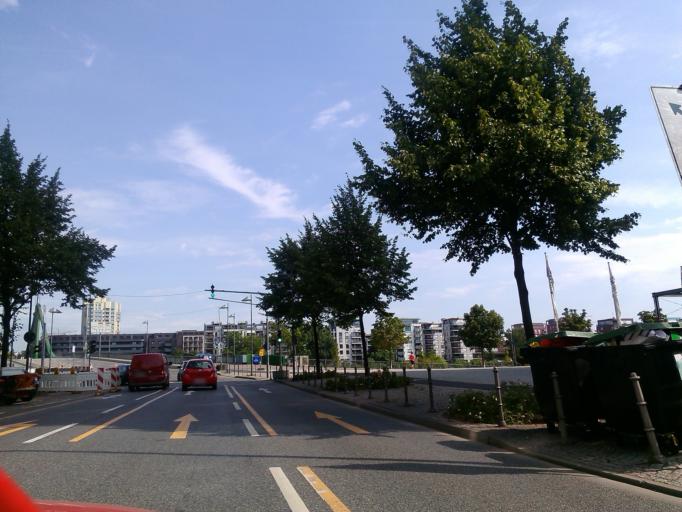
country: DE
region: Hesse
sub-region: Regierungsbezirk Darmstadt
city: Frankfurt am Main
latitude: 50.1058
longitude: 8.6954
